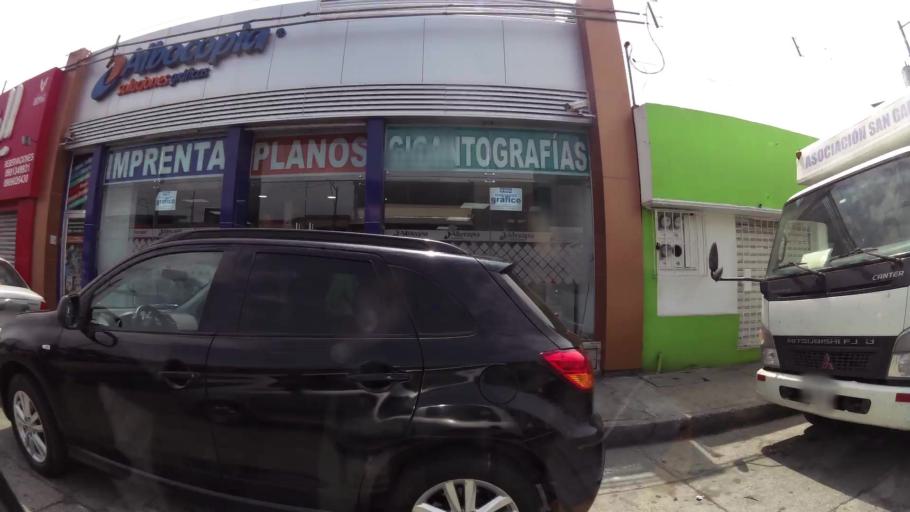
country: EC
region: Guayas
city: Eloy Alfaro
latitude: -2.1465
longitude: -79.8992
